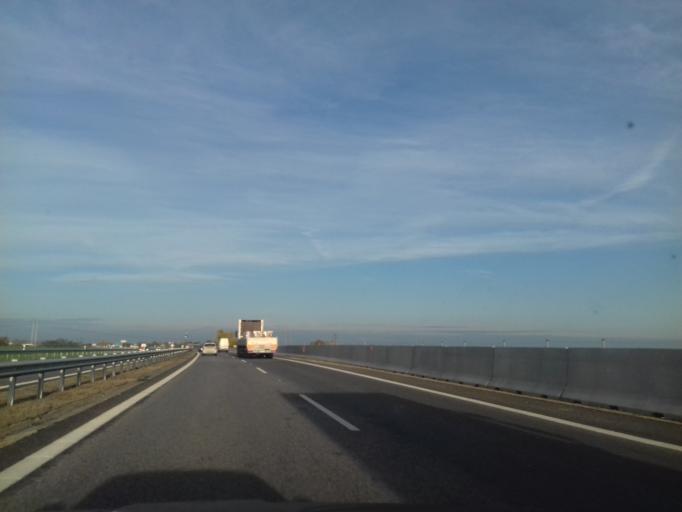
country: SK
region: Trnavsky
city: Sladkovicovo
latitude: 48.2934
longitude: 17.6791
